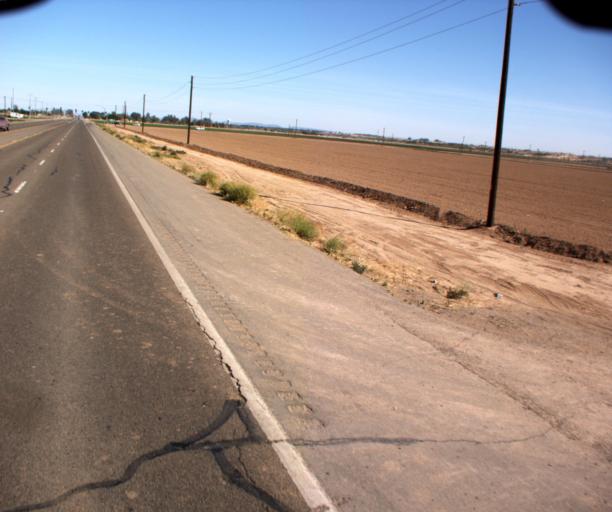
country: US
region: Arizona
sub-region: Yuma County
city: Somerton
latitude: 32.6224
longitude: -114.6497
